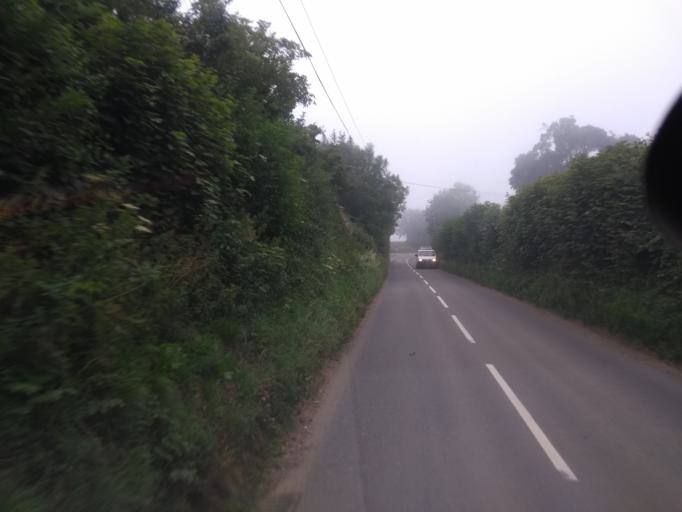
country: GB
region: England
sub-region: Dorset
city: Bridport
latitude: 50.7761
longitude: -2.7730
